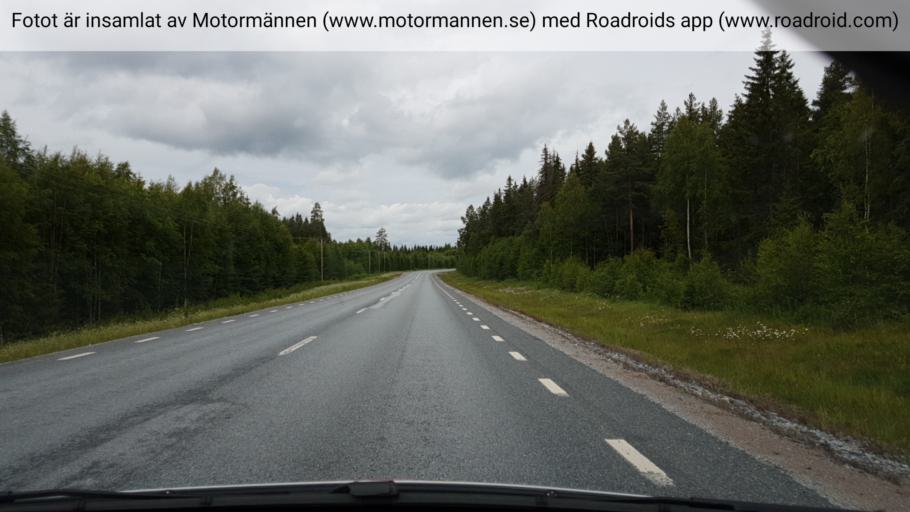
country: SE
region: Vaesternorrland
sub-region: Solleftea Kommun
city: Solleftea
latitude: 63.3611
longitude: 17.0200
